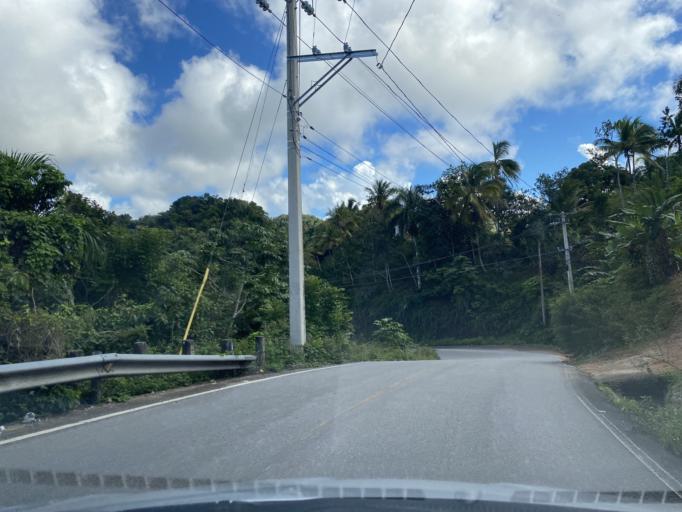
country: DO
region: Samana
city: Las Terrenas
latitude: 19.2684
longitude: -69.5625
